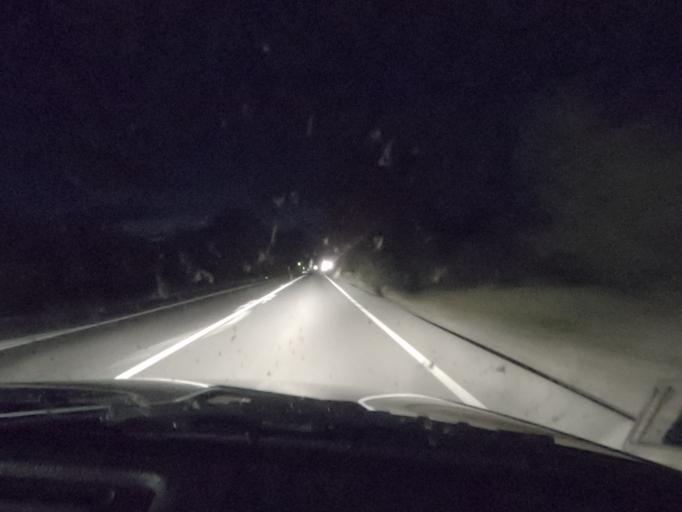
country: ES
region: Extremadura
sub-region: Provincia de Caceres
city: Moraleja
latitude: 40.0751
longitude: -6.6644
